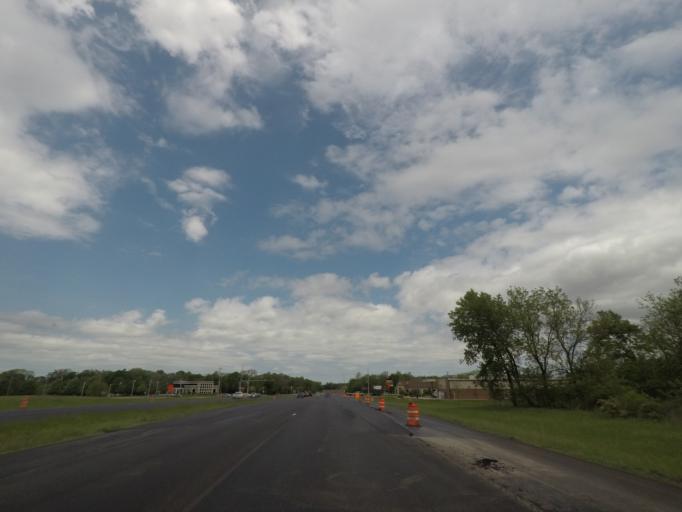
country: US
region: Illinois
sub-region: Winnebago County
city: Roscoe
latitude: 42.4114
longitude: -89.0125
